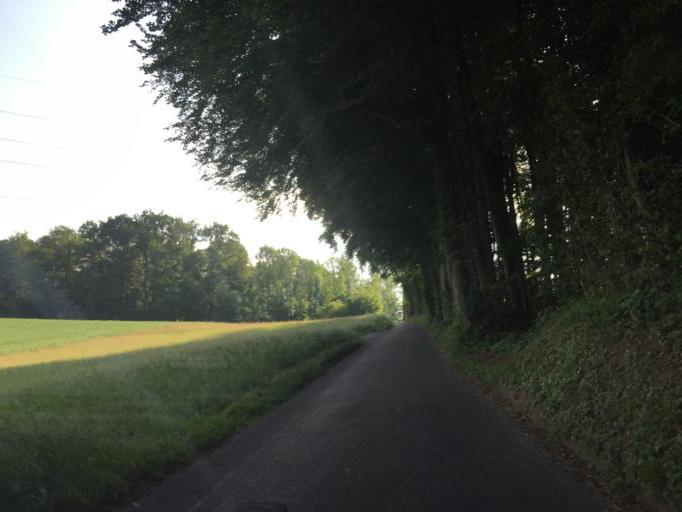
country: CH
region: Zurich
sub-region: Bezirk Buelach
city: Buelach / Gstueckt
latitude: 47.5317
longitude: 8.5599
